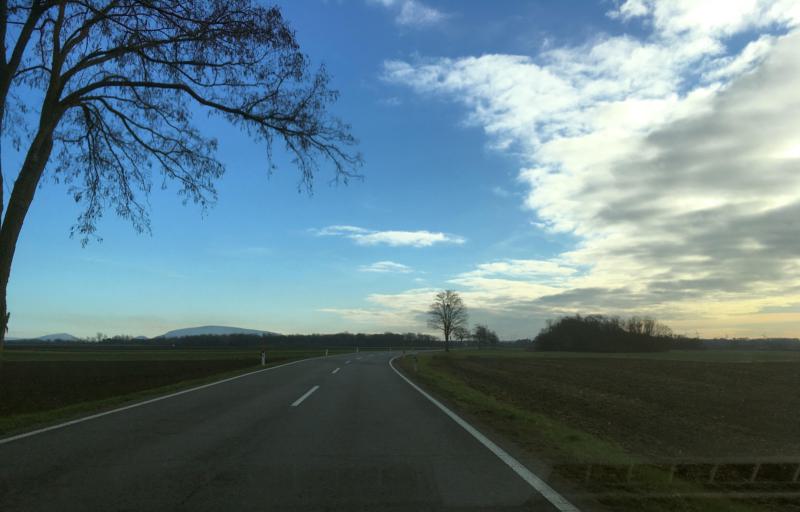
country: AT
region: Lower Austria
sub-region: Politischer Bezirk Ganserndorf
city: Eckartsau
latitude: 48.1543
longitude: 16.7741
